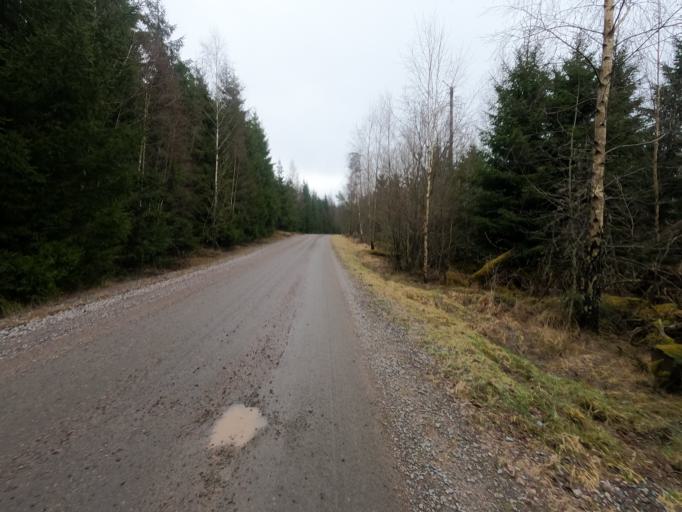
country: SE
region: Kronoberg
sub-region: Markaryds Kommun
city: Stromsnasbruk
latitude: 56.8168
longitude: 13.5674
